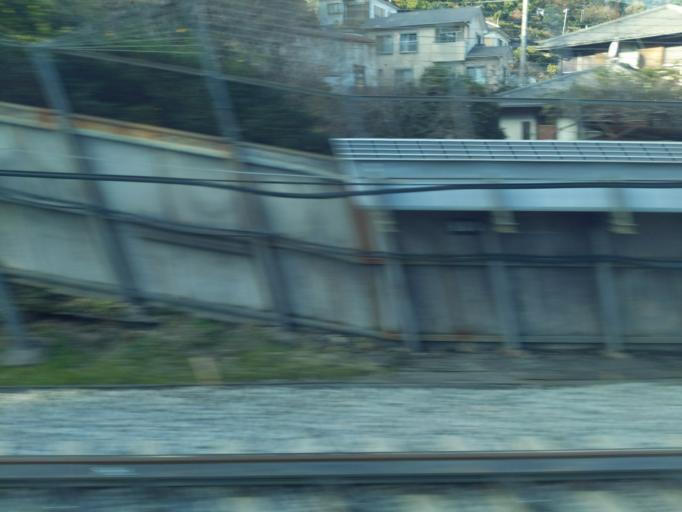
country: JP
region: Kanagawa
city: Yugawara
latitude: 35.1559
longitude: 139.1076
